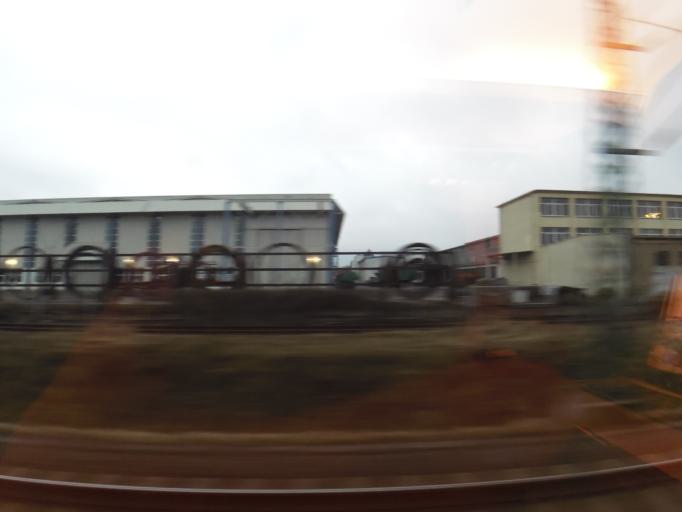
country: DE
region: Saxony
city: Taucha
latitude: 51.3443
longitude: 12.4553
